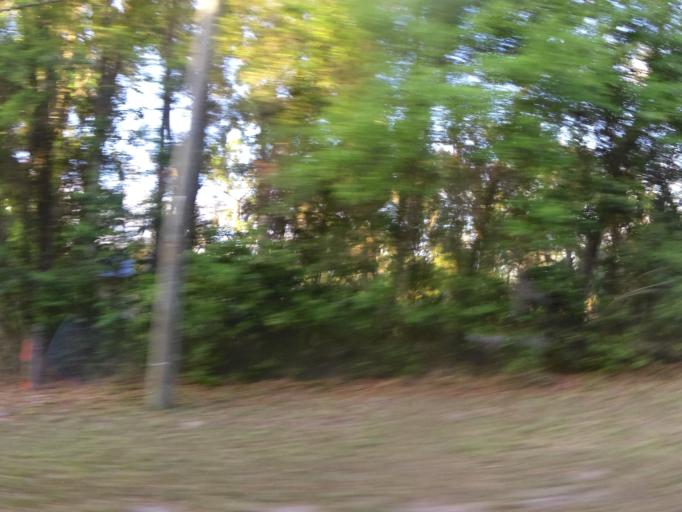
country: US
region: Florida
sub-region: Saint Johns County
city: Fruit Cove
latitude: 30.1253
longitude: -81.5962
